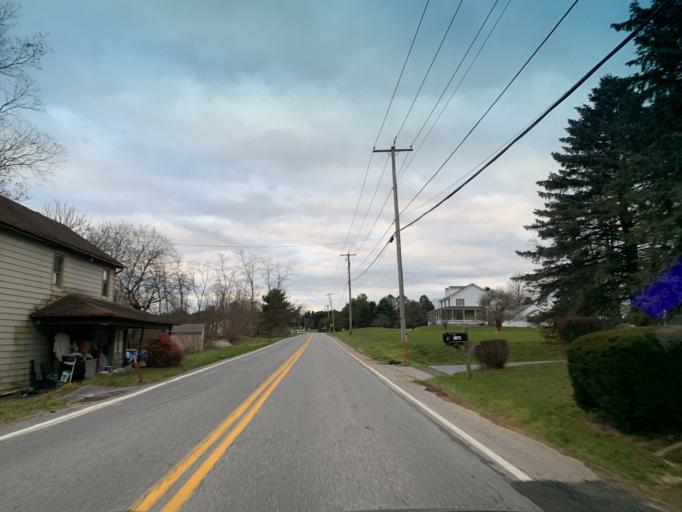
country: US
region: Pennsylvania
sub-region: York County
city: Shrewsbury
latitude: 39.7854
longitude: -76.6618
